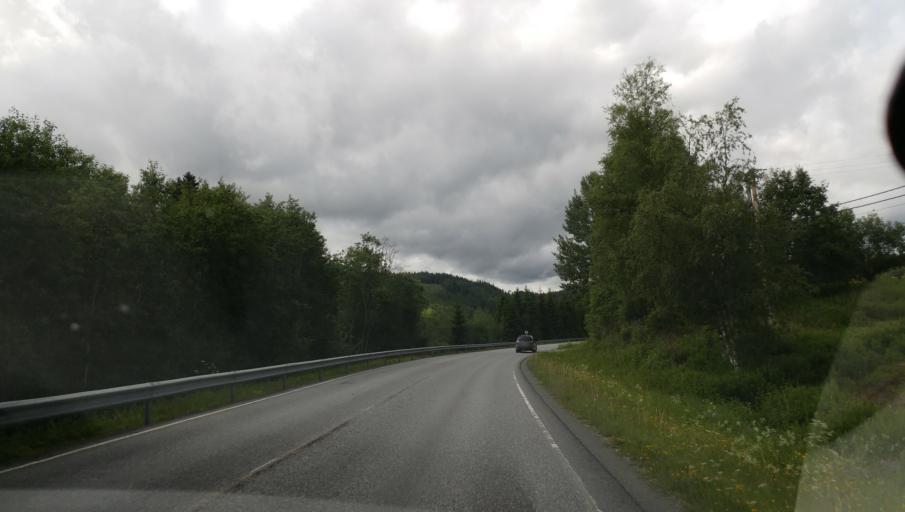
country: NO
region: Nord-Trondelag
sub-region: Stjordal
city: Stjordalshalsen
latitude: 63.3925
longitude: 11.0003
